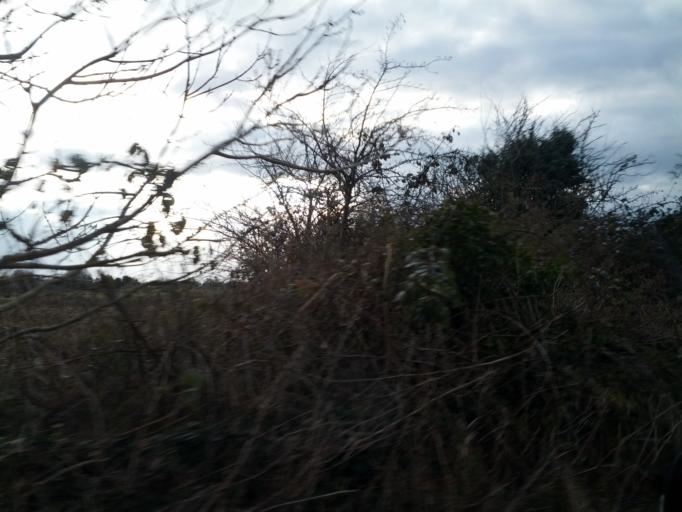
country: IE
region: Connaught
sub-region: County Galway
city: Athenry
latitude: 53.3526
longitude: -8.6684
